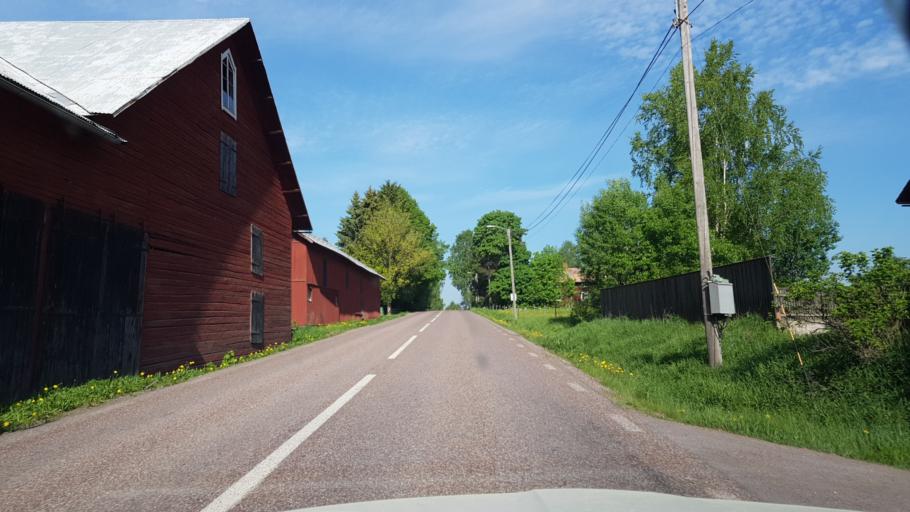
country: SE
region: Dalarna
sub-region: Saters Kommun
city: Saeter
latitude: 60.4148
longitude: 15.7695
